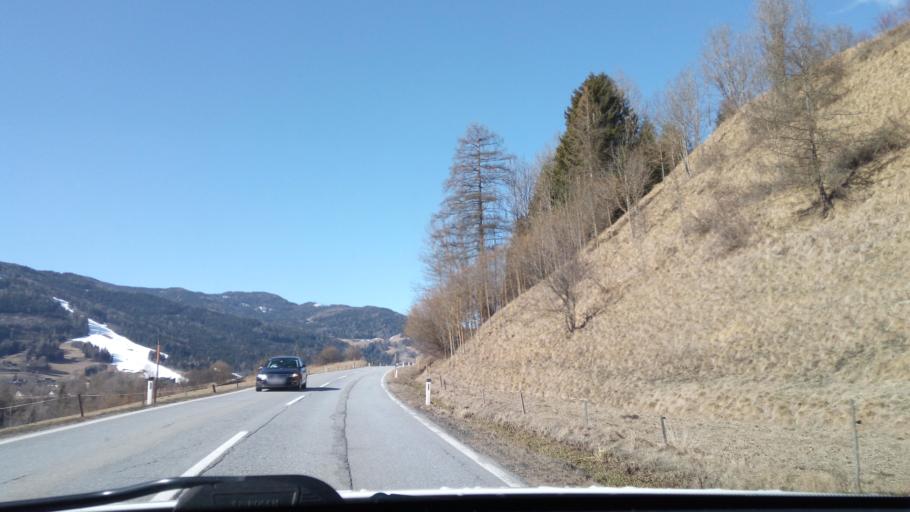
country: AT
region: Styria
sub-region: Politischer Bezirk Murau
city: Sankt Georgen ob Murau
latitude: 47.1051
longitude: 14.1089
